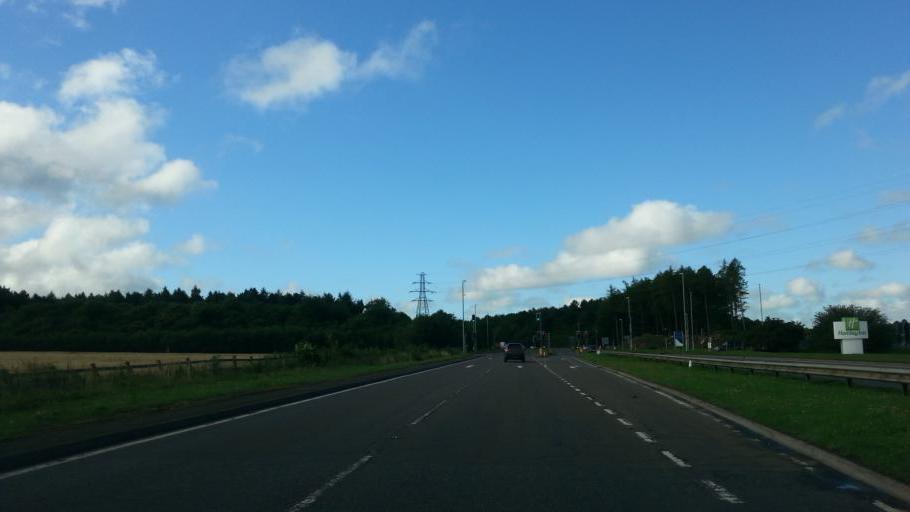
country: GB
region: England
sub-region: Northamptonshire
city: Corby
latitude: 52.4825
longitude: -0.6582
